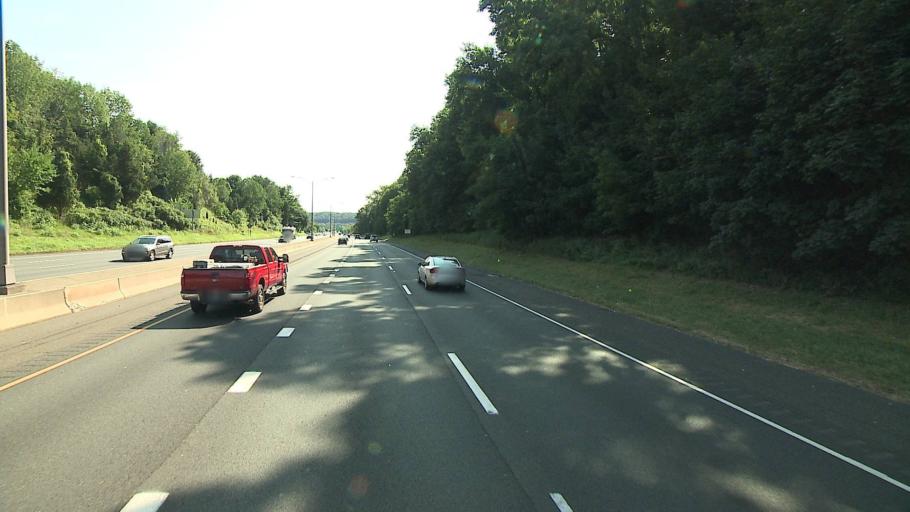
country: US
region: Connecticut
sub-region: Fairfield County
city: Danbury
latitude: 41.4135
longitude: -73.4426
